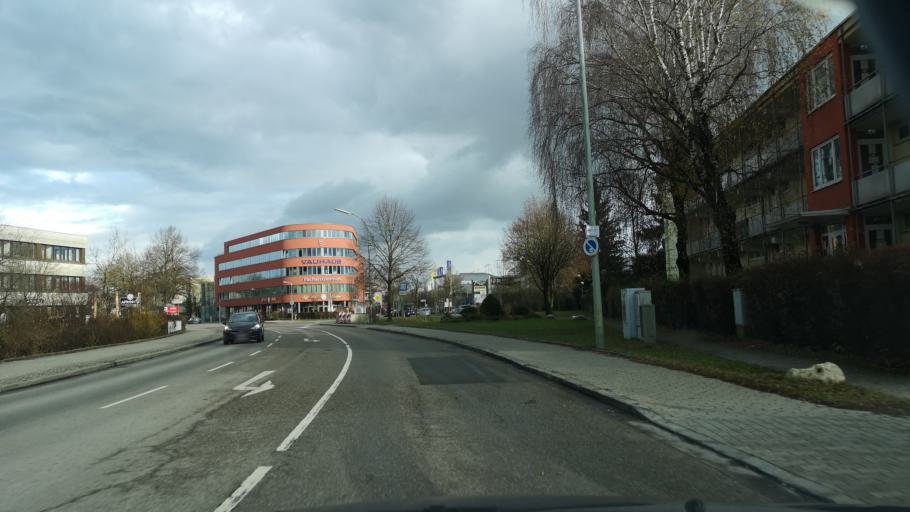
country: DE
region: Bavaria
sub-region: Upper Bavaria
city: Poing
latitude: 48.1706
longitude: 11.8040
